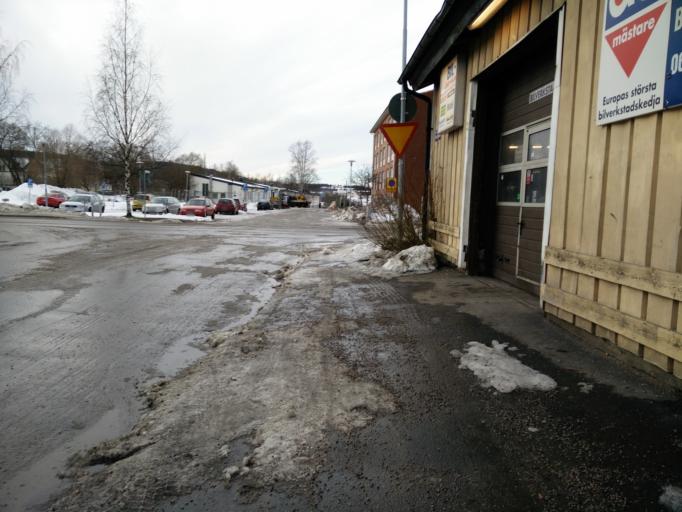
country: SE
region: Vaesternorrland
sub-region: Sundsvalls Kommun
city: Sundsvall
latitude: 62.3906
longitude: 17.2878
